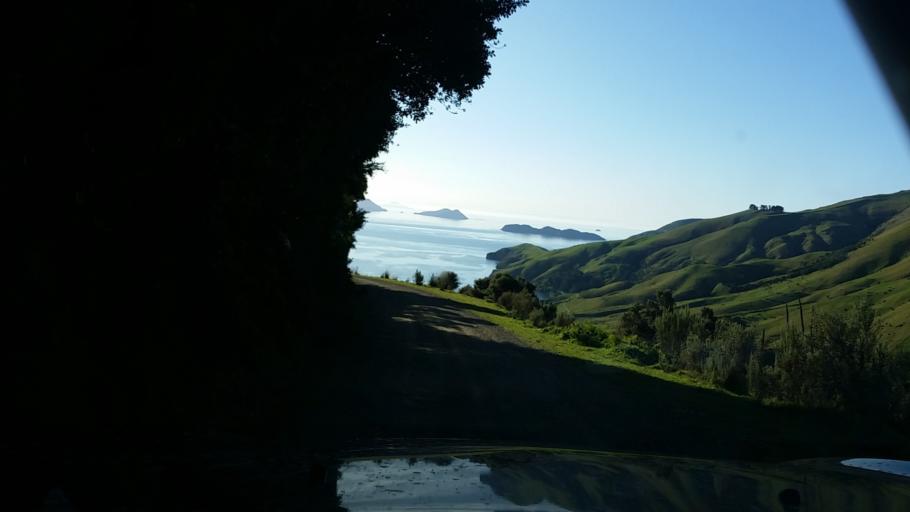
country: NZ
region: Marlborough
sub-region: Marlborough District
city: Picton
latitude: -41.0260
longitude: 174.1492
